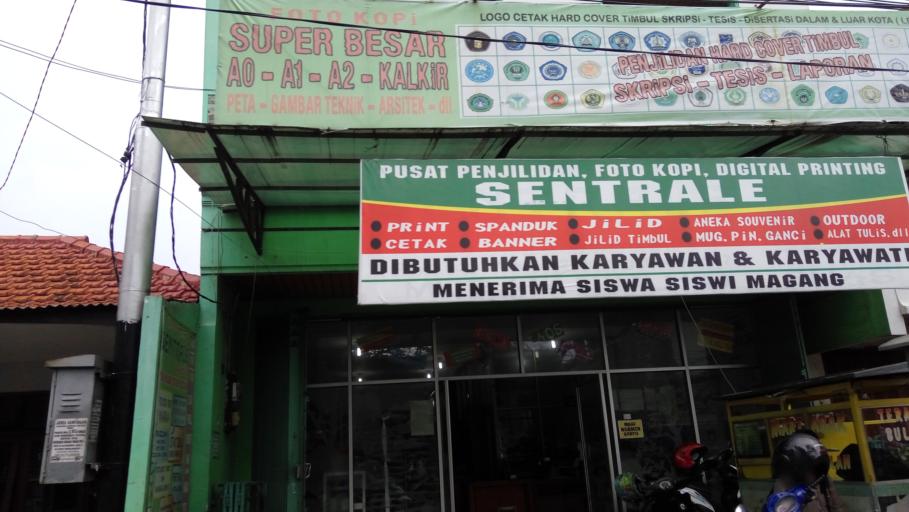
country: ID
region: East Java
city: Malang
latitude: -7.9365
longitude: 112.6058
